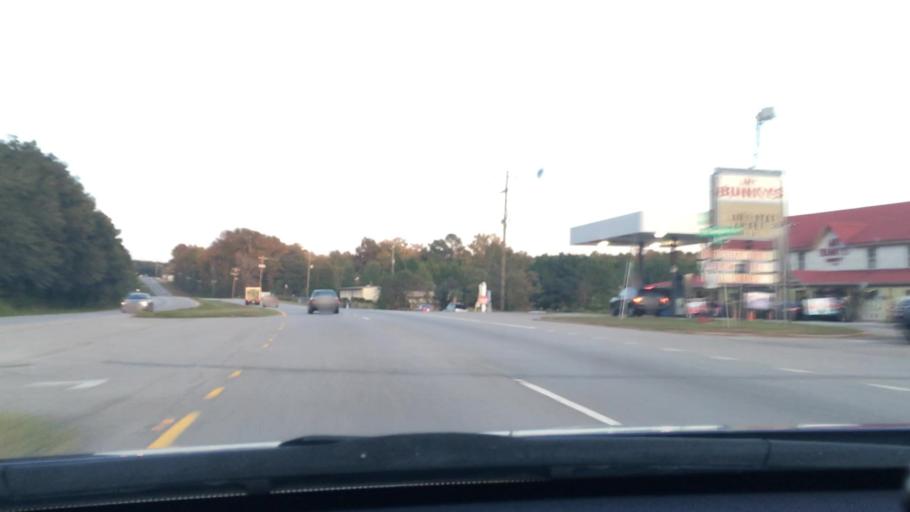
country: US
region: South Carolina
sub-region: Richland County
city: Gadsden
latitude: 33.9392
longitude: -80.7866
